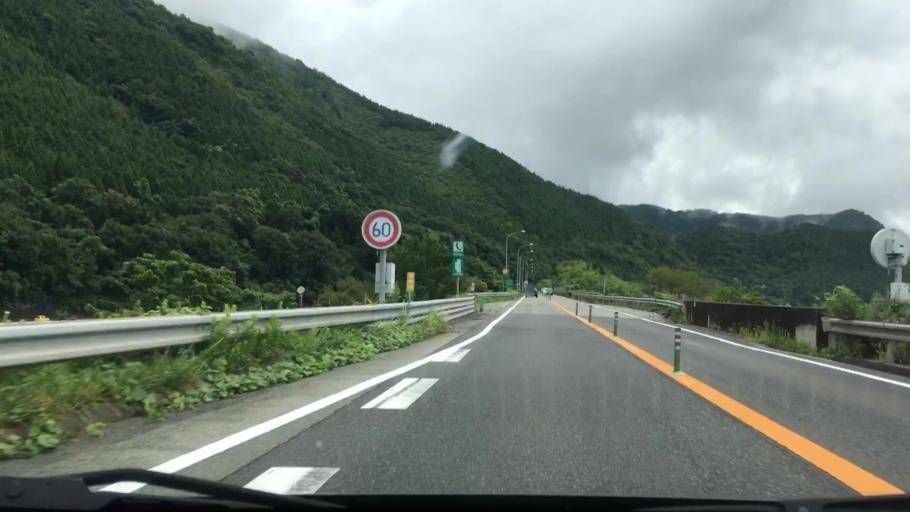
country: JP
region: Hyogo
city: Nishiwaki
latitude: 35.0445
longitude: 134.7669
